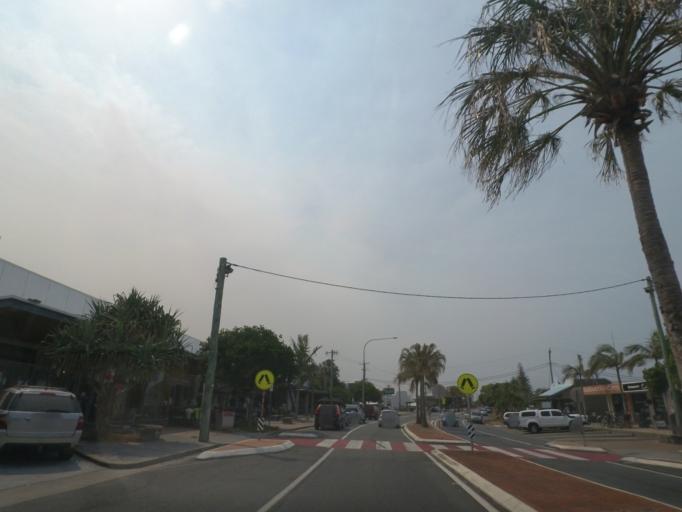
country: AU
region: New South Wales
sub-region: Tweed
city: Casuarina
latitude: -28.3321
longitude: 153.5696
